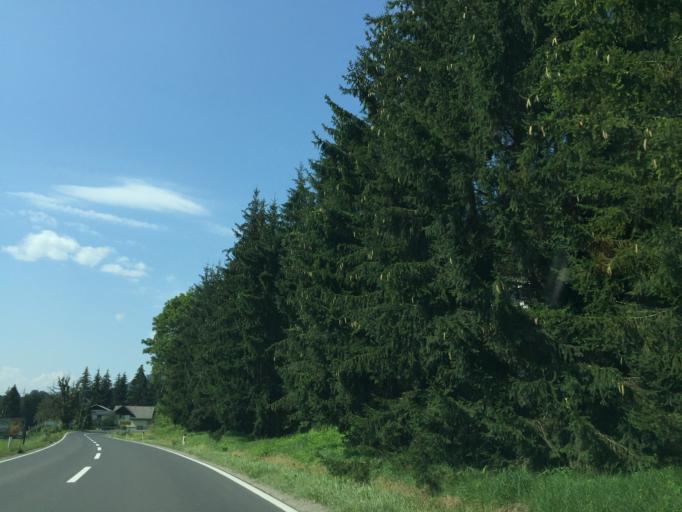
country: SI
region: Dravograd
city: Dravograd
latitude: 46.5741
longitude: 15.0310
